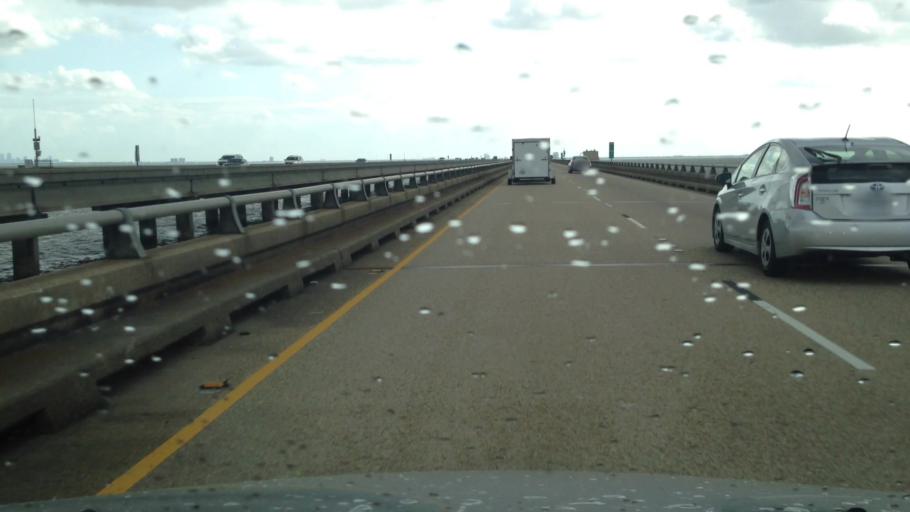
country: US
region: Louisiana
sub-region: Jefferson Parish
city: Metairie
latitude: 30.1117
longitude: -90.1383
